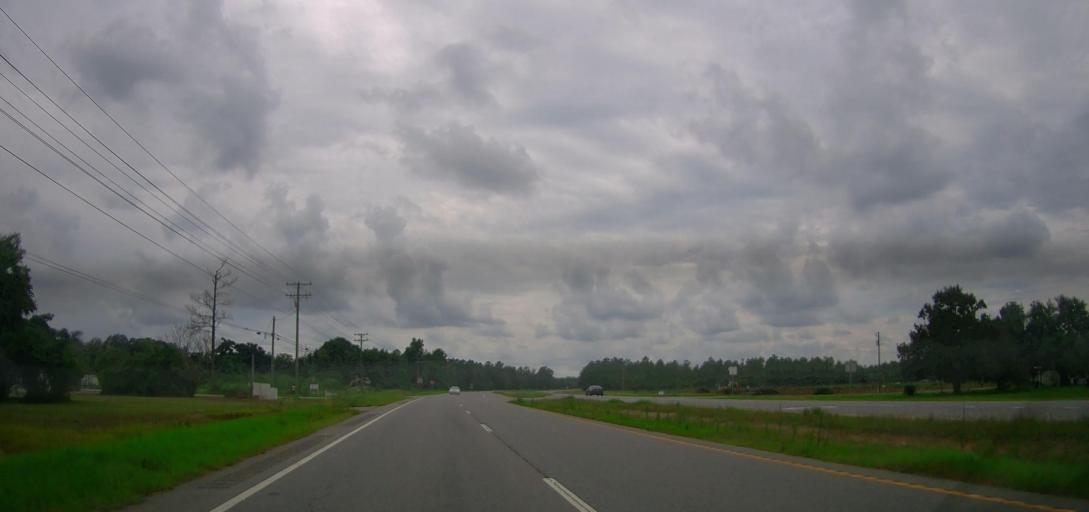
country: US
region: Georgia
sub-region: Appling County
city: Baxley
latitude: 31.8132
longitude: -82.4506
